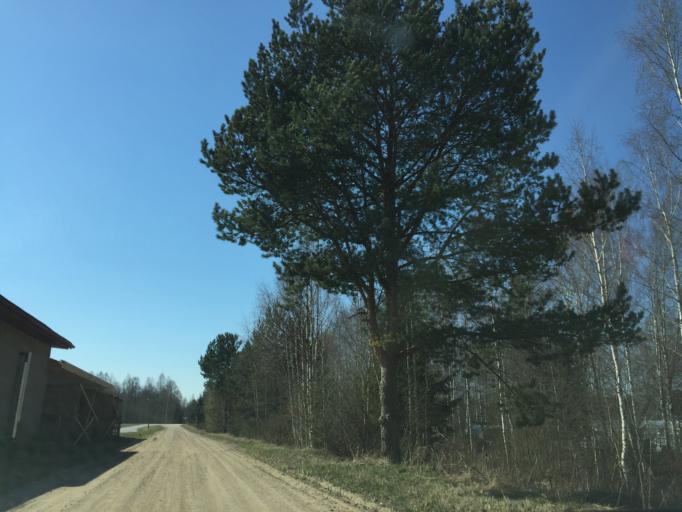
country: EE
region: Jogevamaa
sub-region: Mustvee linn
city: Mustvee
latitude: 58.7818
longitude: 26.9378
